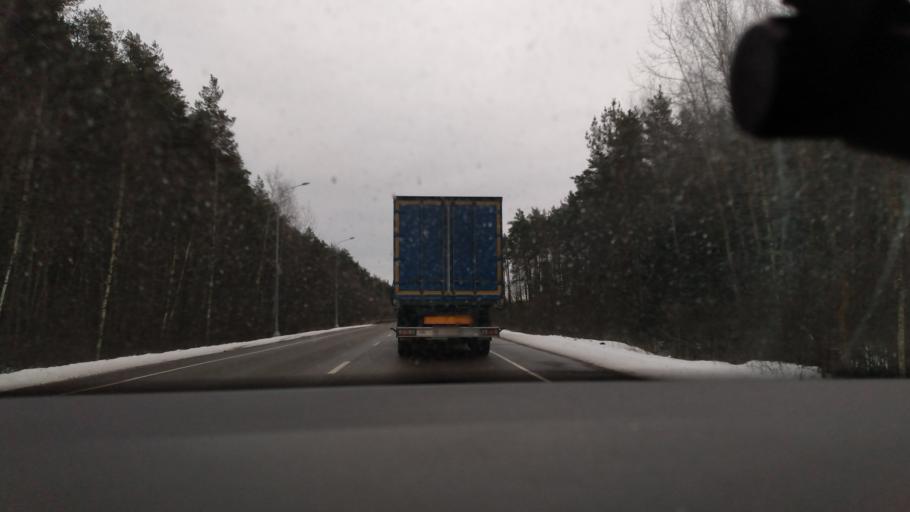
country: RU
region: Moskovskaya
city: Yegor'yevsk
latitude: 55.4512
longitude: 39.0032
